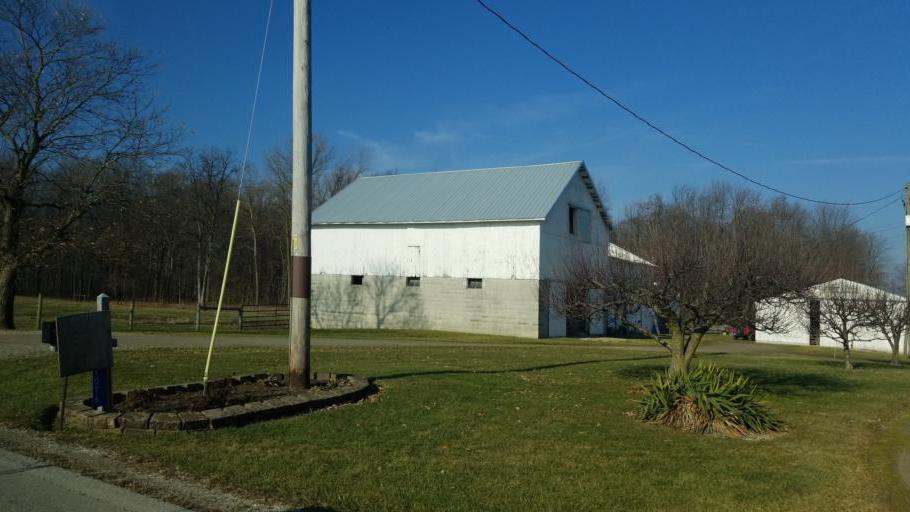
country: US
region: Ohio
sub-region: Crawford County
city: Bucyrus
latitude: 40.9067
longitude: -83.0613
